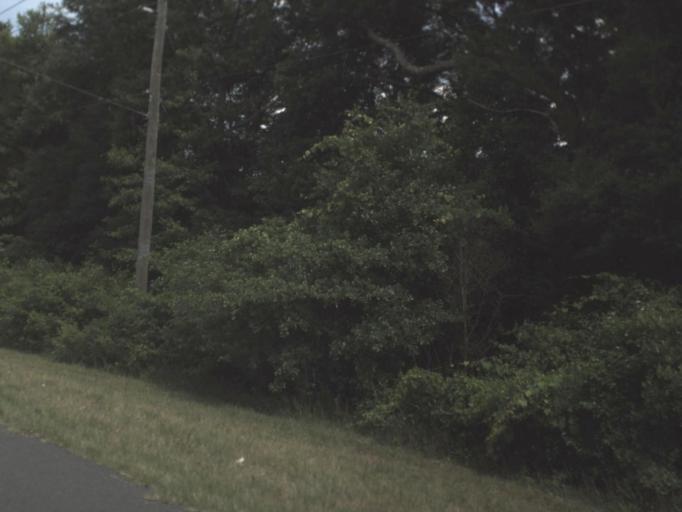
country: US
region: Florida
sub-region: Putnam County
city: Interlachen
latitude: 29.6228
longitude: -81.9552
